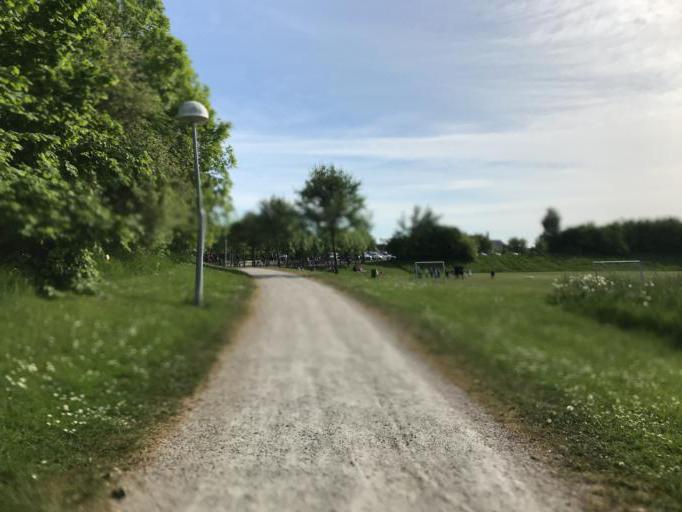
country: SE
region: Skane
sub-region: Malmo
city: Oxie
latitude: 55.5331
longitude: 13.0934
